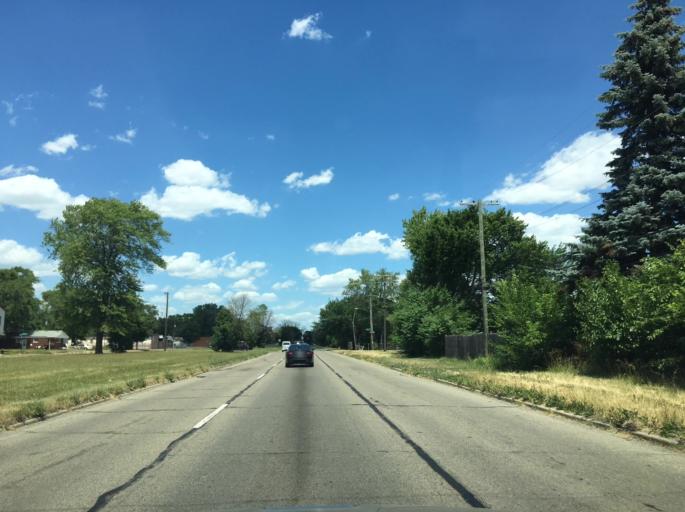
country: US
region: Michigan
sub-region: Wayne County
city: Hamtramck
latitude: 42.4290
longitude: -83.0432
